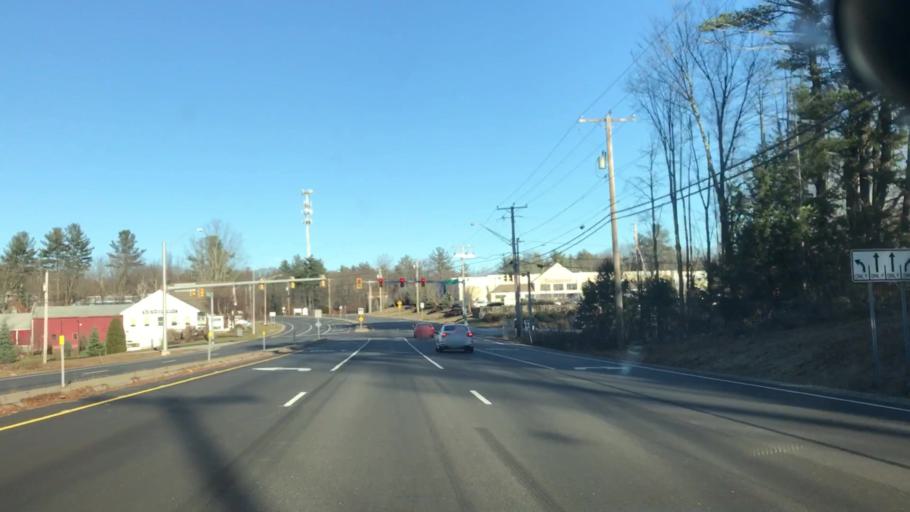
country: US
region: New Hampshire
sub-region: Hillsborough County
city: Bedford
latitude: 42.9212
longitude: -71.5386
